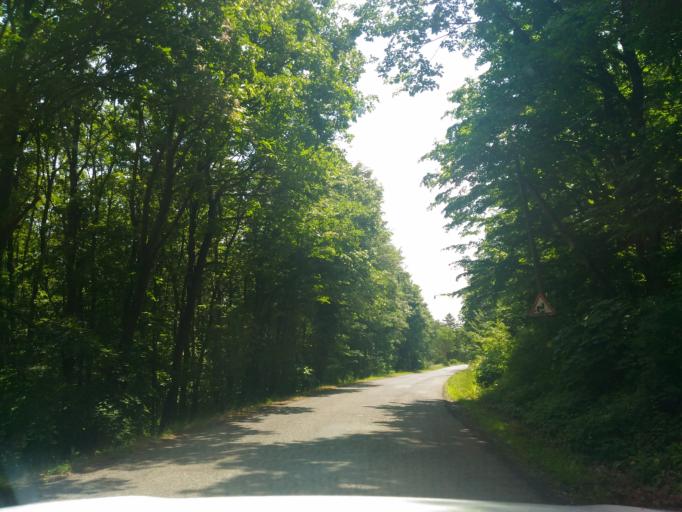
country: HU
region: Baranya
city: Pecs
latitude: 46.1324
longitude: 18.2346
